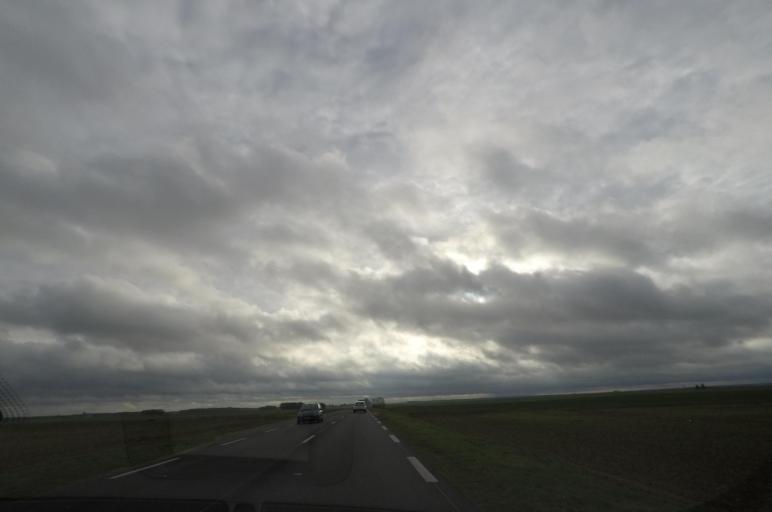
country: FR
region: Centre
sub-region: Departement du Loir-et-Cher
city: Herbault
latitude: 47.7068
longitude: 1.1700
